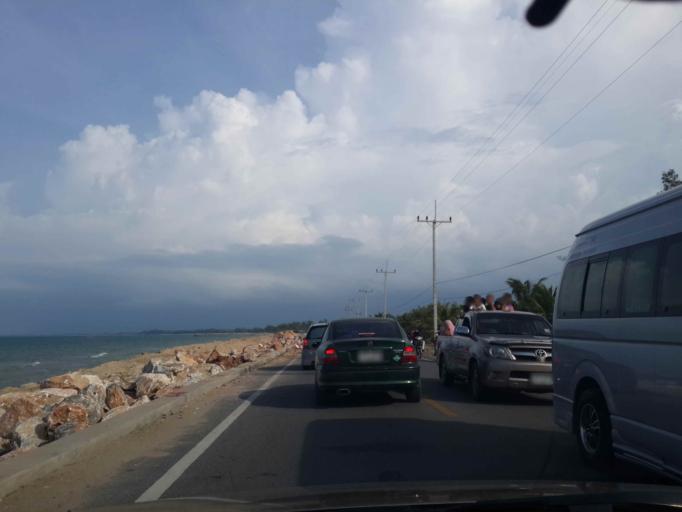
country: TH
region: Pattani
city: Yaring
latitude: 6.9254
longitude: 101.3277
